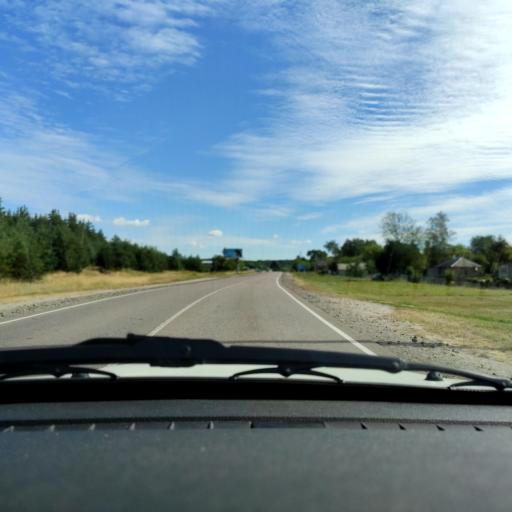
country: RU
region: Voronezj
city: Uglyanets
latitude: 51.8521
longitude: 39.6616
